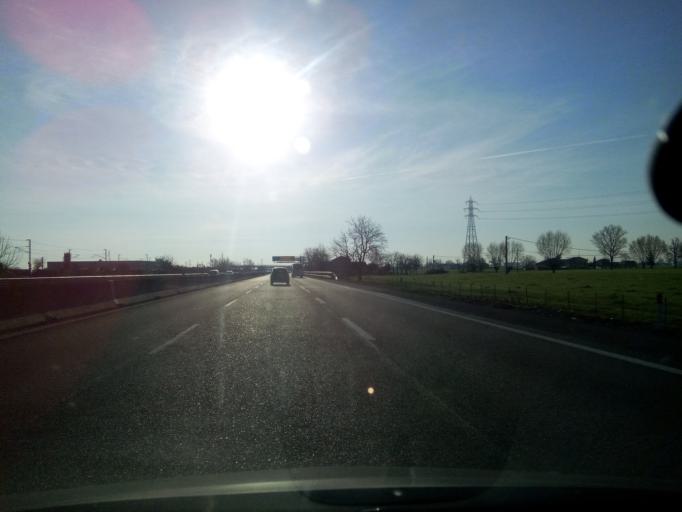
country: IT
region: Emilia-Romagna
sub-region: Provincia di Parma
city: Fontanellato
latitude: 44.8713
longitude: 10.2006
